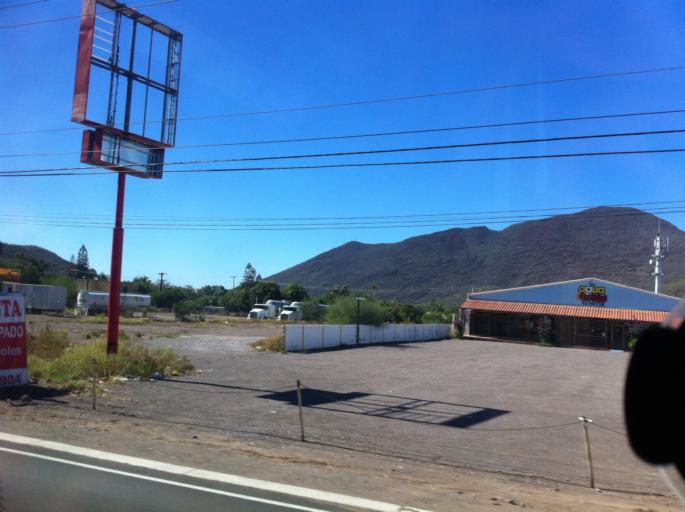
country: MX
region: Sonora
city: Heroica Guaymas
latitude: 27.9435
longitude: -110.9330
